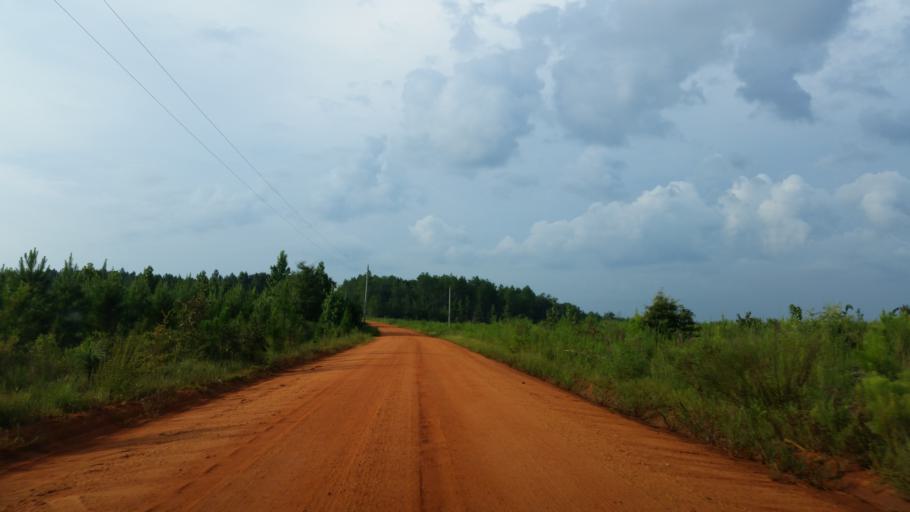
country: US
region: Alabama
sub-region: Escambia County
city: Atmore
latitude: 30.8589
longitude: -87.5783
